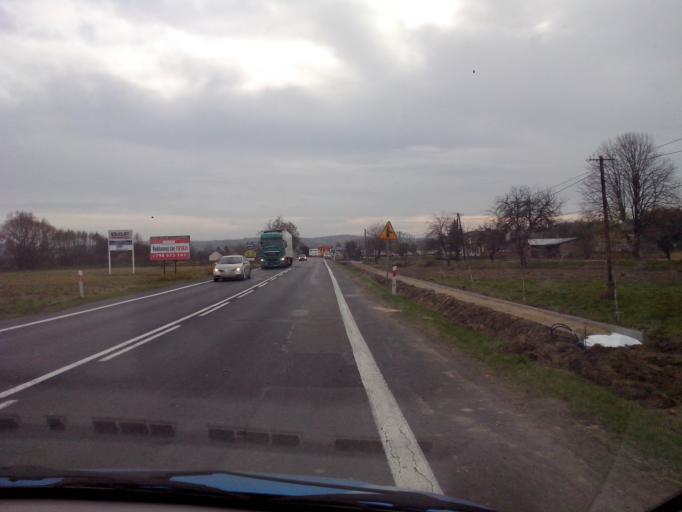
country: PL
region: Subcarpathian Voivodeship
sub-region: Powiat rzeszowski
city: Lutoryz
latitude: 49.9592
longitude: 21.9170
